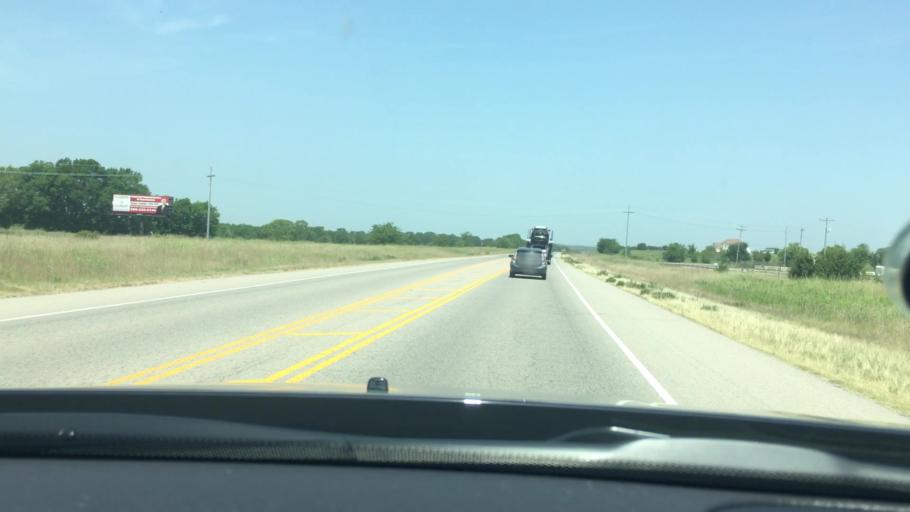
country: US
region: Oklahoma
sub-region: Pontotoc County
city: Ada
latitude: 34.7094
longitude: -96.6151
